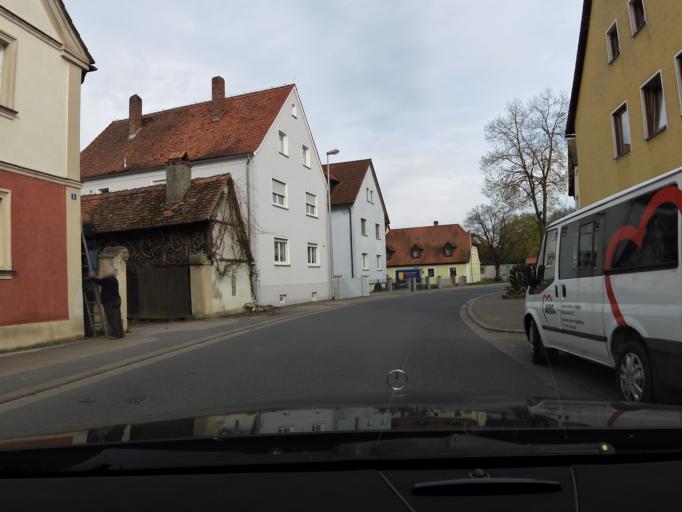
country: DE
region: Bavaria
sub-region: Upper Franconia
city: Pommersfelden
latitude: 49.7670
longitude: 10.8210
